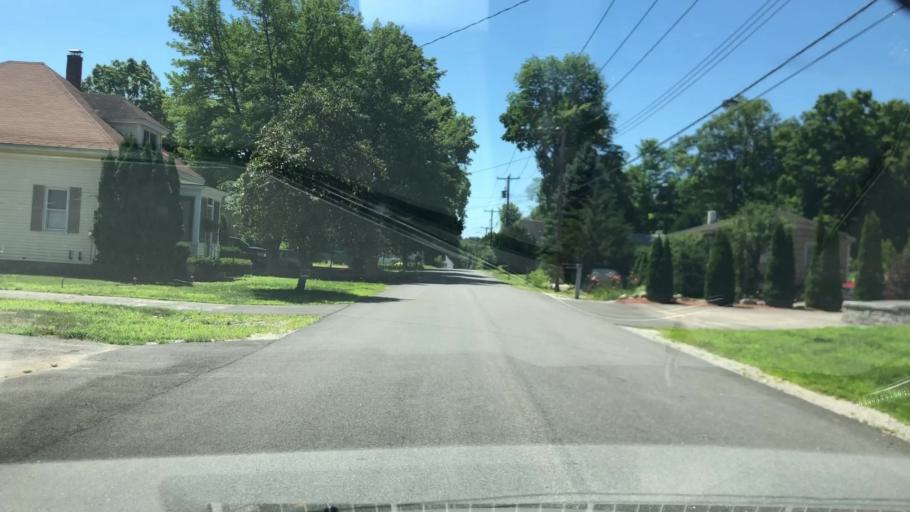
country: US
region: New Hampshire
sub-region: Hillsborough County
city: Milford
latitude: 42.8374
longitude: -71.6367
